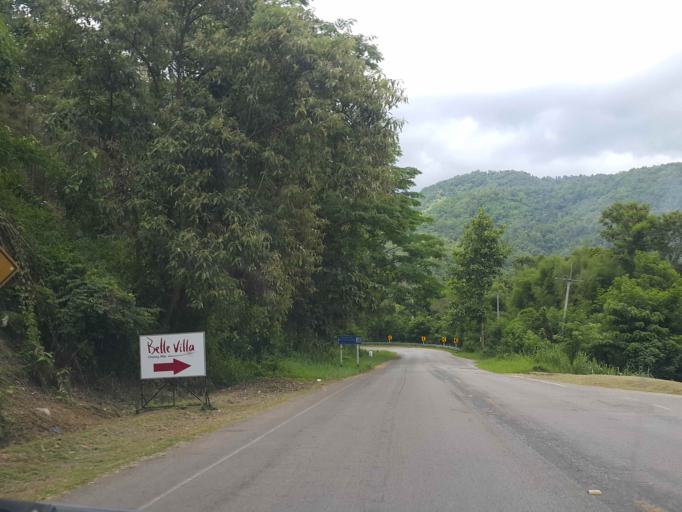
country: TH
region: Chiang Mai
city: Samoeng
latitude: 18.8012
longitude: 98.8306
